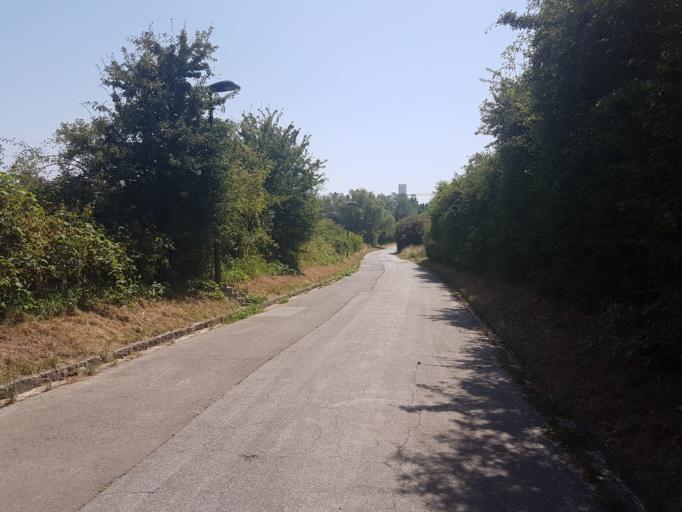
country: LU
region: Luxembourg
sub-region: Canton de Luxembourg
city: Luxembourg
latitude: 49.5858
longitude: 6.1098
